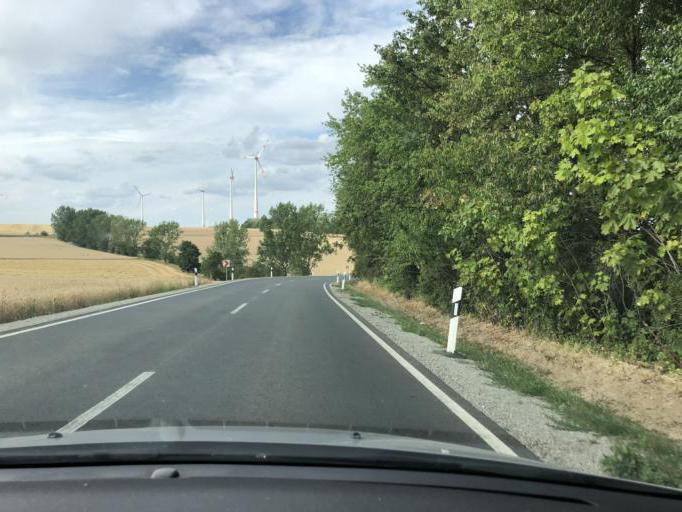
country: DE
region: Thuringia
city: Schmiedehausen
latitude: 51.0405
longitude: 11.6470
